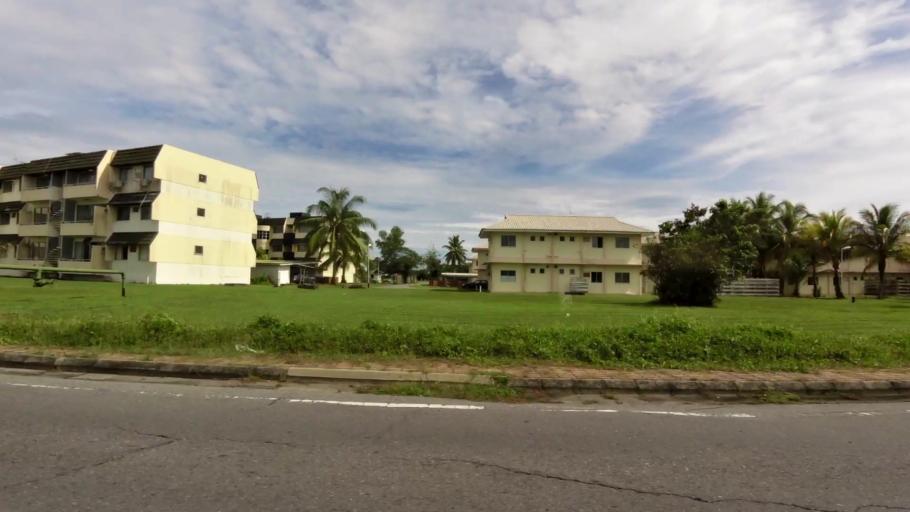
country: BN
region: Belait
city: Seria
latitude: 4.6134
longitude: 114.3230
